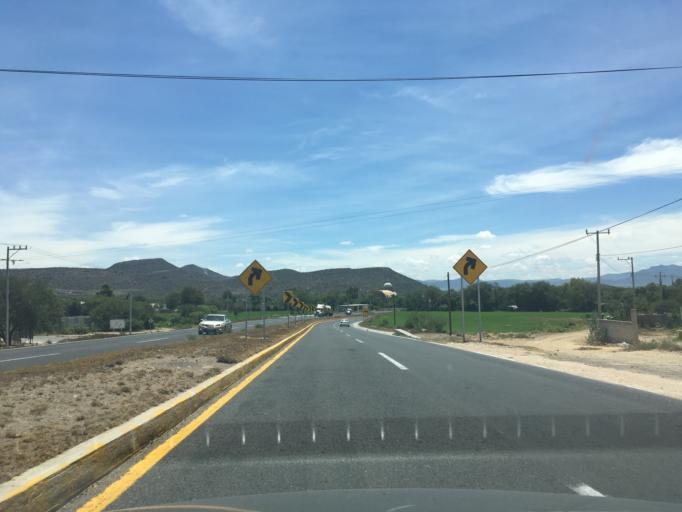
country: MX
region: Hidalgo
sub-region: Tasquillo
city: Portezuelo
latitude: 20.4858
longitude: -99.3113
